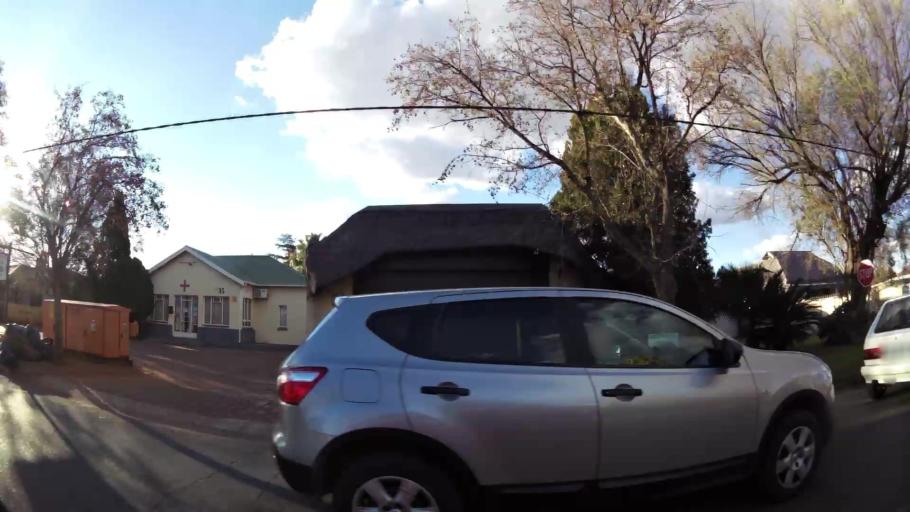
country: ZA
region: North-West
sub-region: Dr Kenneth Kaunda District Municipality
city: Potchefstroom
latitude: -26.7075
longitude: 27.0994
